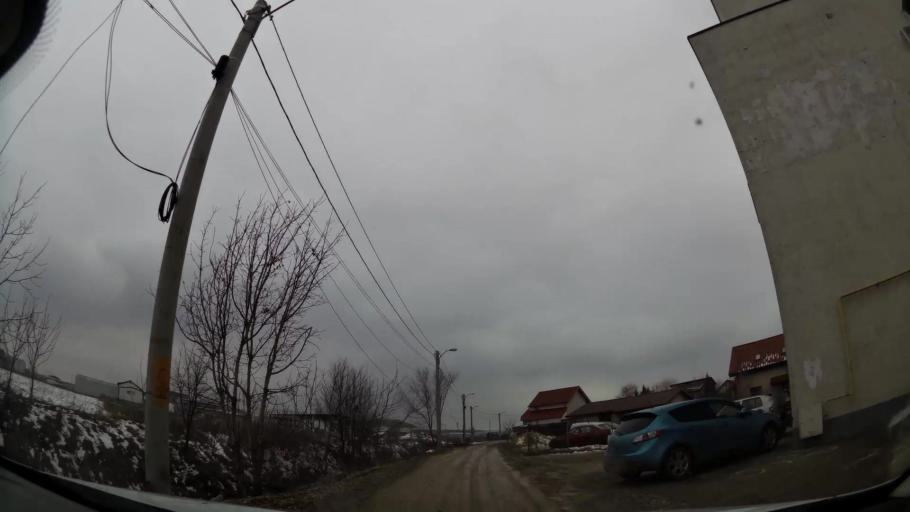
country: RO
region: Ilfov
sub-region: Comuna Otopeni
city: Otopeni
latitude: 44.5478
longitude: 26.0907
